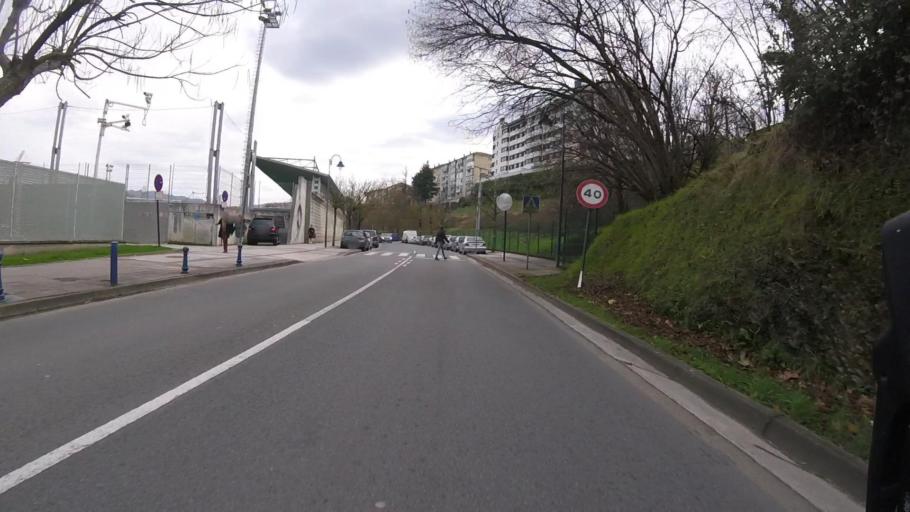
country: ES
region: Basque Country
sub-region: Provincia de Guipuzcoa
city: Errenteria
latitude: 43.3105
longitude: -1.8951
